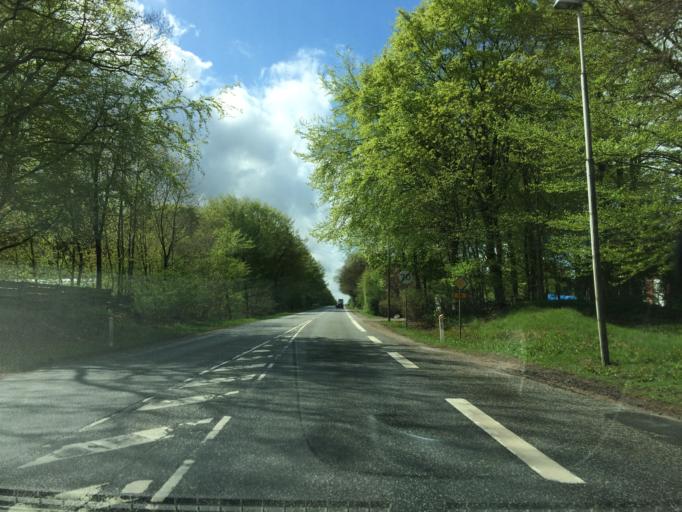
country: DK
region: Central Jutland
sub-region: Viborg Kommune
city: Stoholm
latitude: 56.4263
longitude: 9.0834
